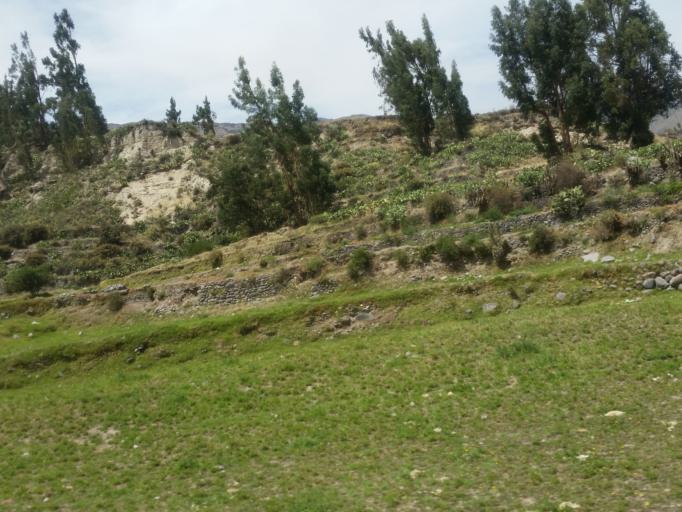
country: PE
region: Arequipa
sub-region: Provincia de Caylloma
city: Maca
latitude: -15.6441
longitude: -71.7486
